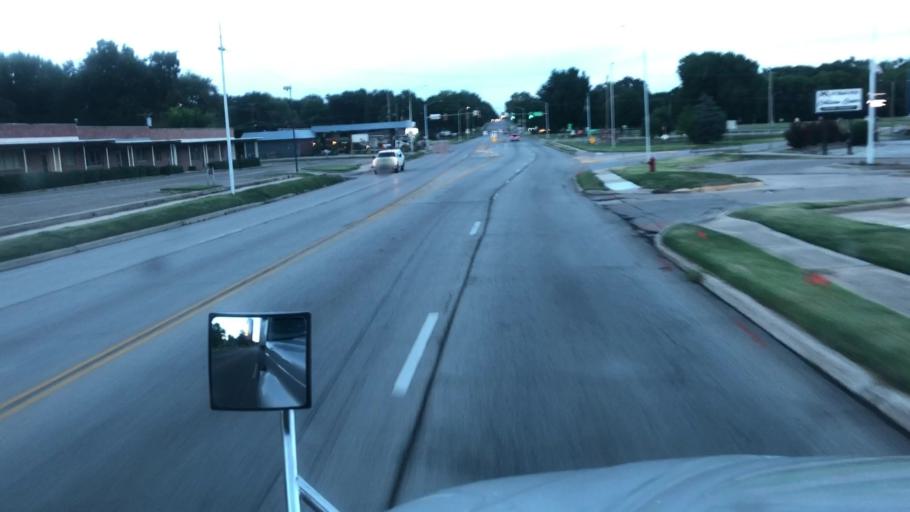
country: US
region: Oklahoma
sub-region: Kay County
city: Ponca City
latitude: 36.7079
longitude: -97.0673
